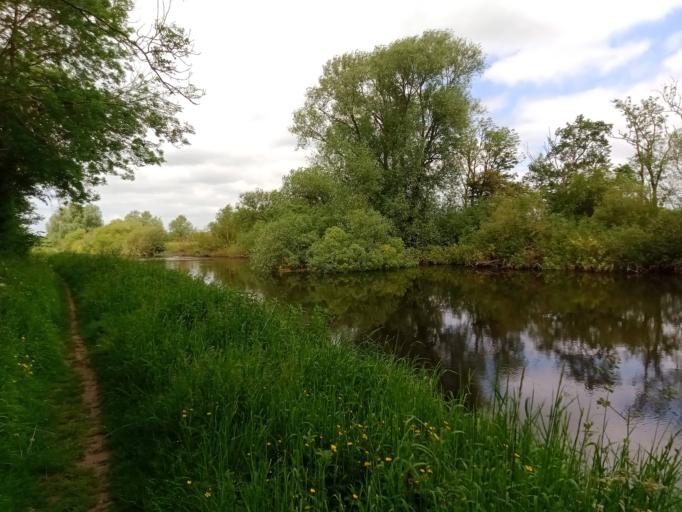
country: IE
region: Leinster
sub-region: County Carlow
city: Carlow
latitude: 52.7995
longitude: -6.9625
